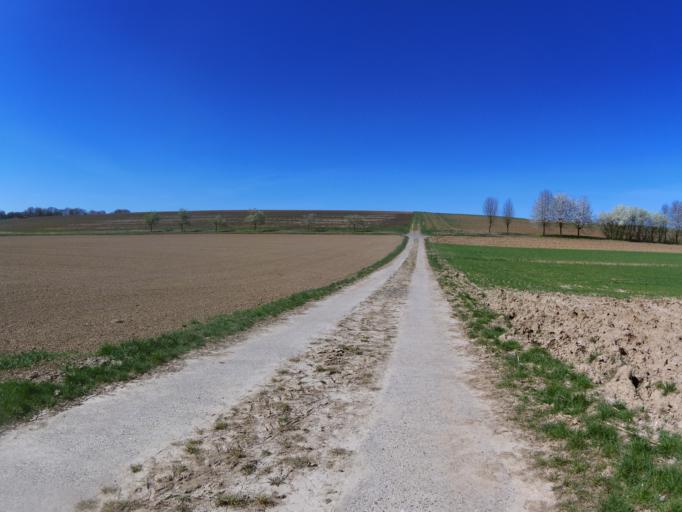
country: DE
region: Bavaria
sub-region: Regierungsbezirk Unterfranken
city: Rottendorf
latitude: 49.8110
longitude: 10.0743
